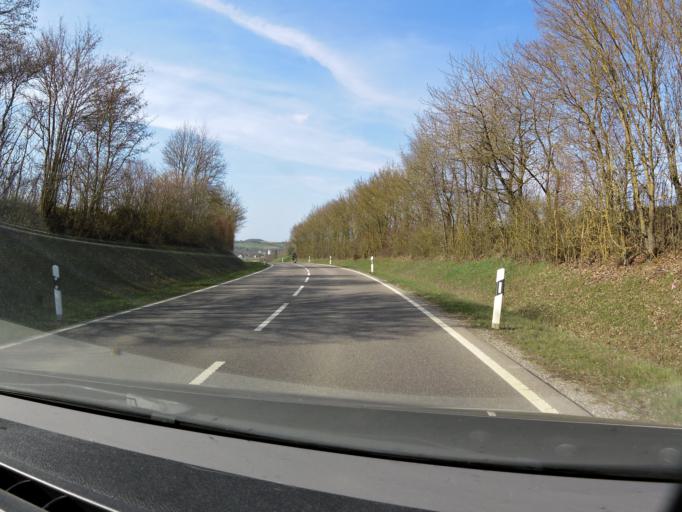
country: DE
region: Bavaria
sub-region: Regierungsbezirk Unterfranken
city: Bieberehren
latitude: 49.5056
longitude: 10.0155
